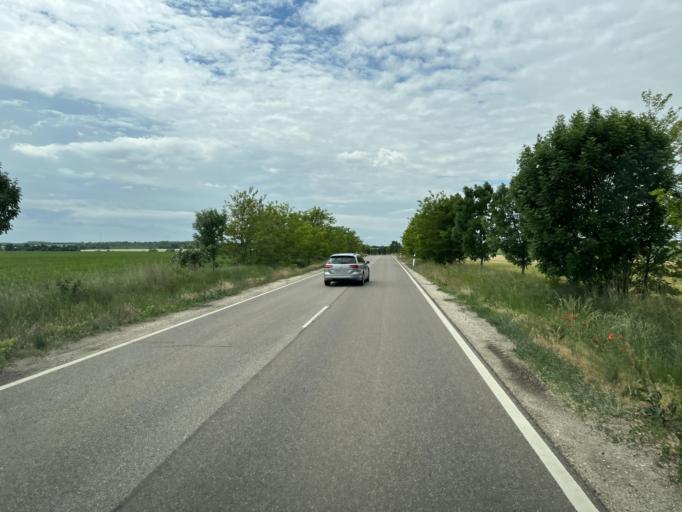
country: HU
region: Pest
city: Koka
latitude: 47.5112
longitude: 19.5968
